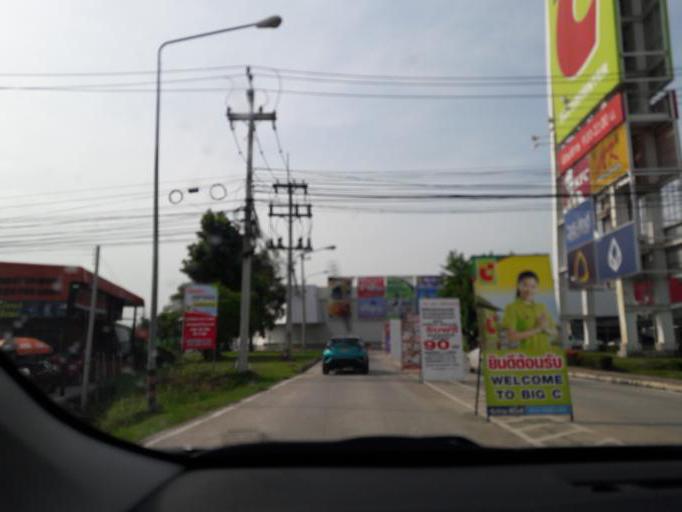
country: TH
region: Ang Thong
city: Ang Thong
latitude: 14.5818
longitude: 100.4590
